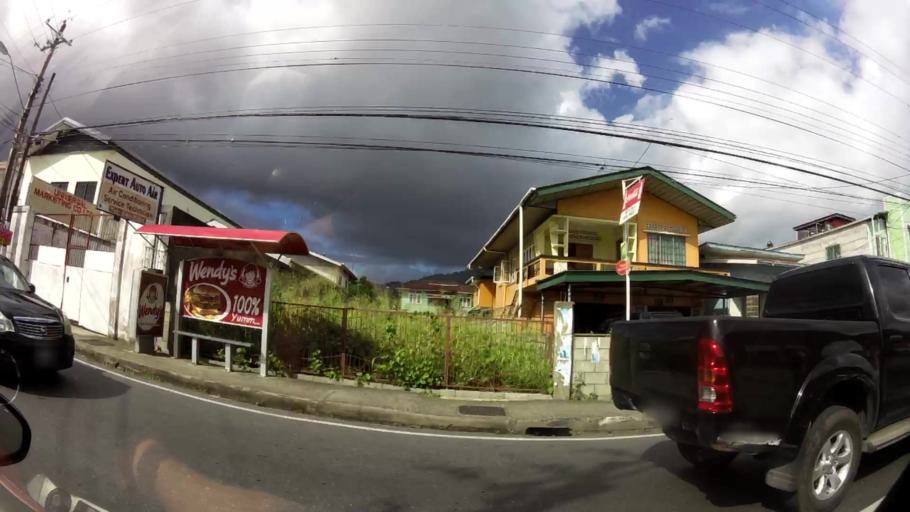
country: TT
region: Tunapuna/Piarco
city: Paradise
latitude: 10.6444
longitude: -61.3644
